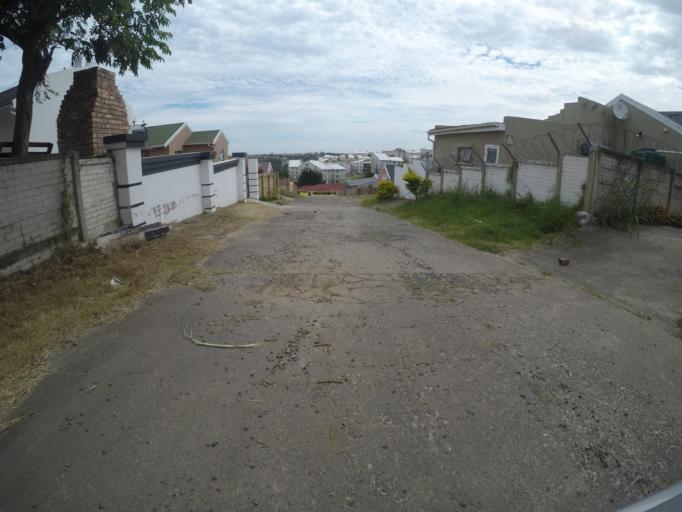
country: ZA
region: Eastern Cape
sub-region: Buffalo City Metropolitan Municipality
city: East London
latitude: -32.9932
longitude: 27.8654
